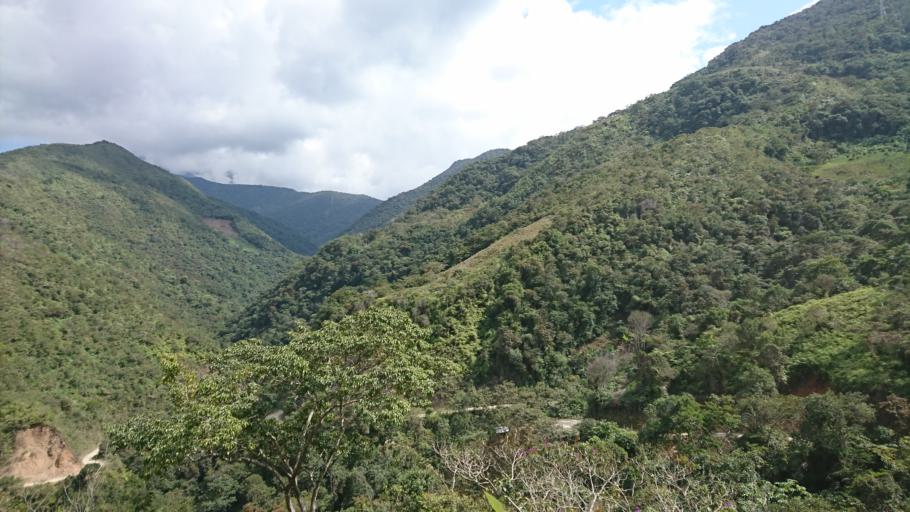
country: BO
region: La Paz
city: Coroico
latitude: -16.0780
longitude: -67.7909
